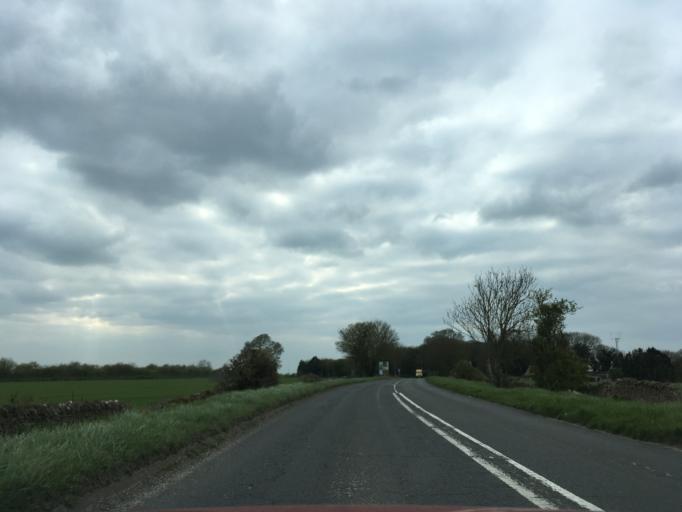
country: GB
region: England
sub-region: Oxfordshire
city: Carterton
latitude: 51.7893
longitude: -1.5771
